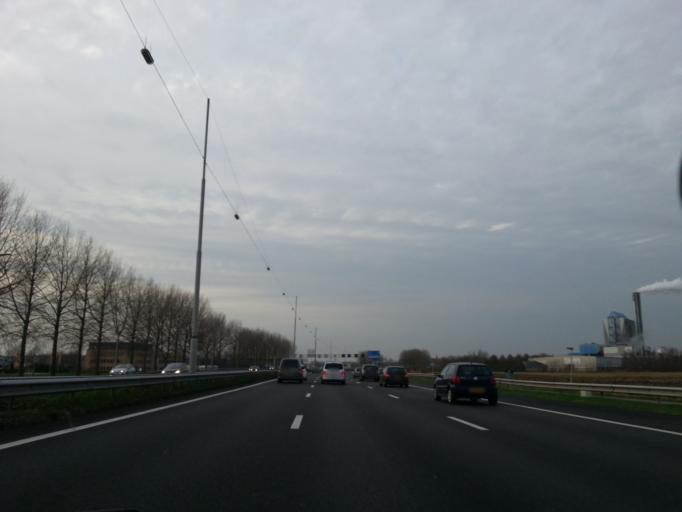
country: NL
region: Gelderland
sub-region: Gemeente Duiven
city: Duiven
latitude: 51.9653
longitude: 6.0066
